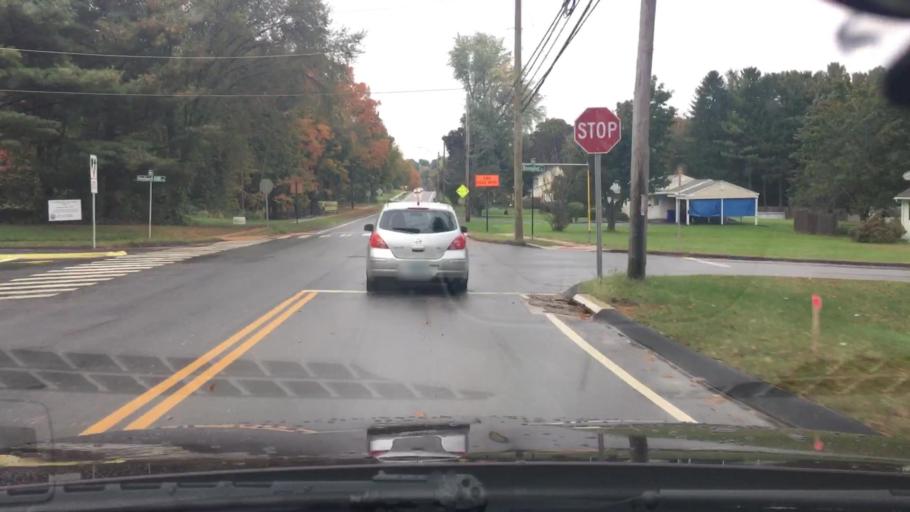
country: US
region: Connecticut
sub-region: Hartford County
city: Manchester
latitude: 41.8208
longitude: -72.5210
